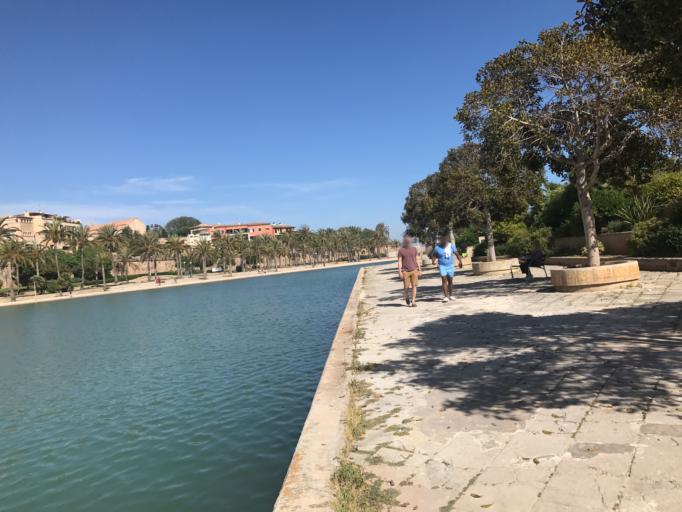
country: ES
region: Balearic Islands
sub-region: Illes Balears
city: Palma
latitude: 39.5657
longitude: 2.6485
